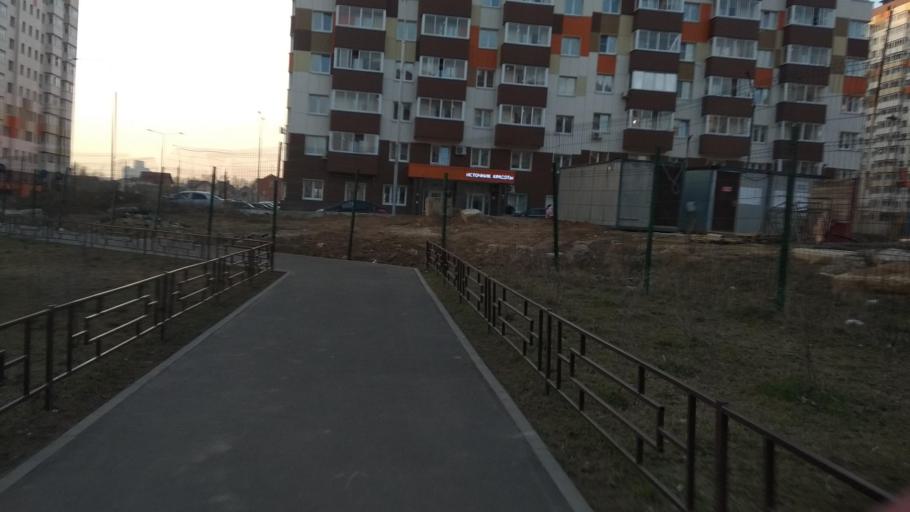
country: RU
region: Moskovskaya
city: Vidnoye
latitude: 55.5600
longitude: 37.7023
